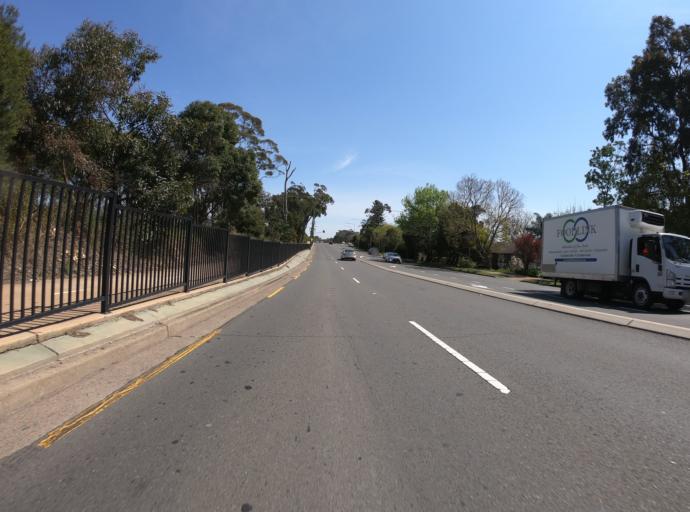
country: AU
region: New South Wales
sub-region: The Hills Shire
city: Castle Hill
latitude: -33.7250
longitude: 150.9877
